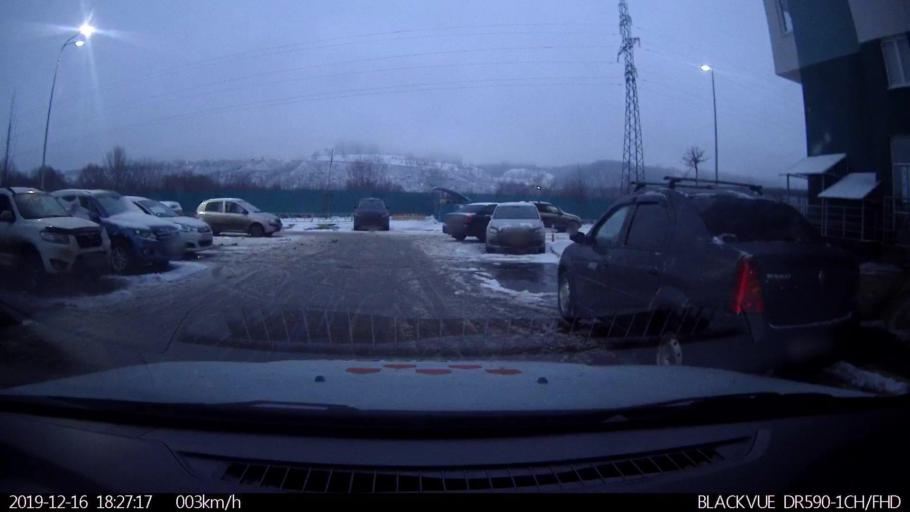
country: RU
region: Nizjnij Novgorod
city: Nizhniy Novgorod
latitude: 56.3016
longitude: 43.9531
